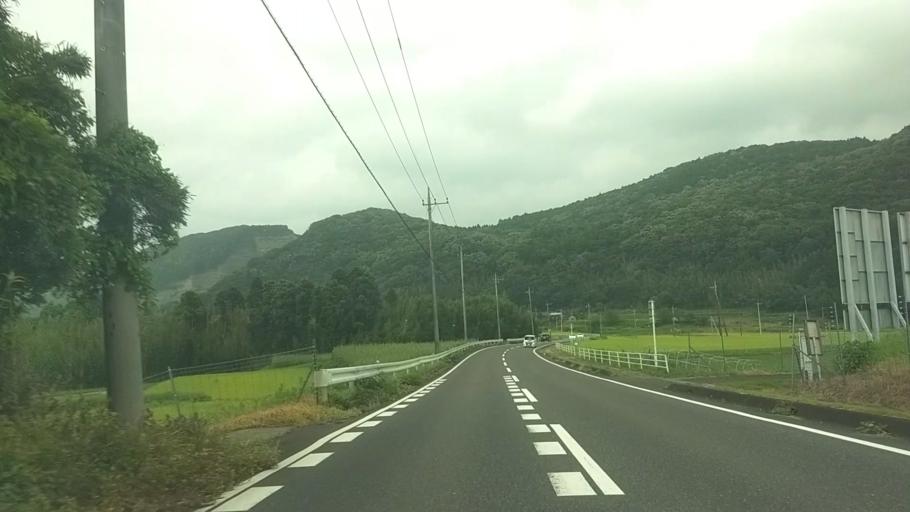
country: JP
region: Chiba
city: Kimitsu
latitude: 35.2602
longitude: 140.0032
